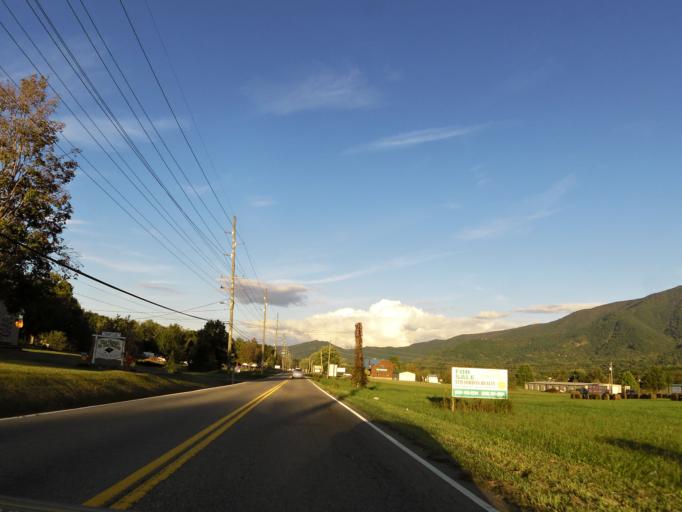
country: US
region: Tennessee
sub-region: Sevier County
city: Pigeon Forge
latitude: 35.7111
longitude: -83.6614
